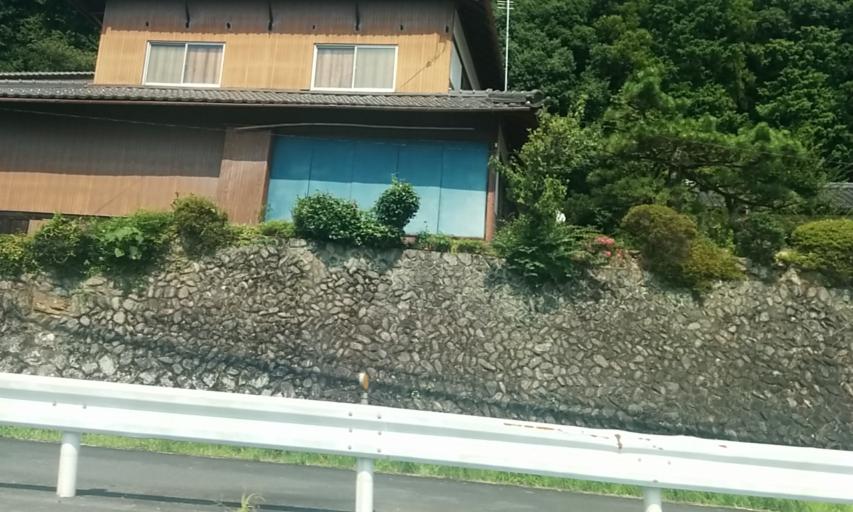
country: JP
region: Kyoto
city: Fukuchiyama
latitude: 35.3280
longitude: 135.1209
